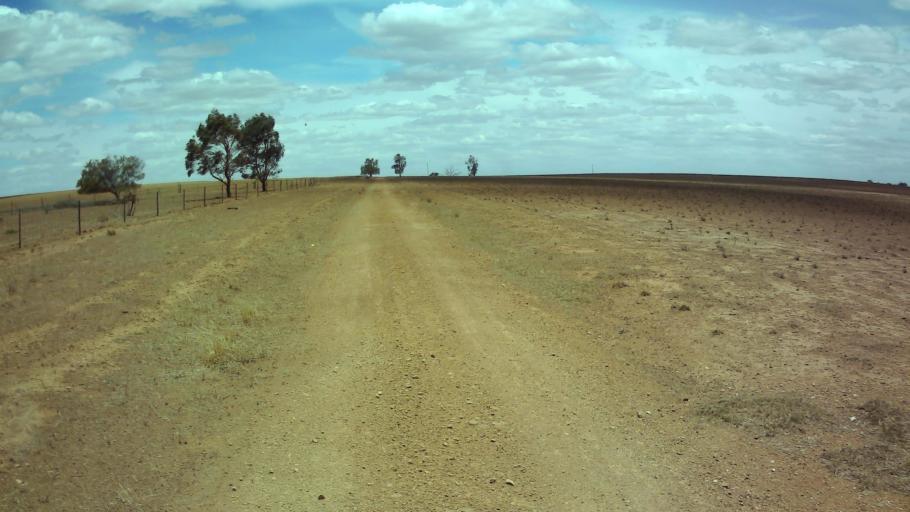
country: AU
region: New South Wales
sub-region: Weddin
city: Grenfell
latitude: -33.8971
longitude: 147.7401
